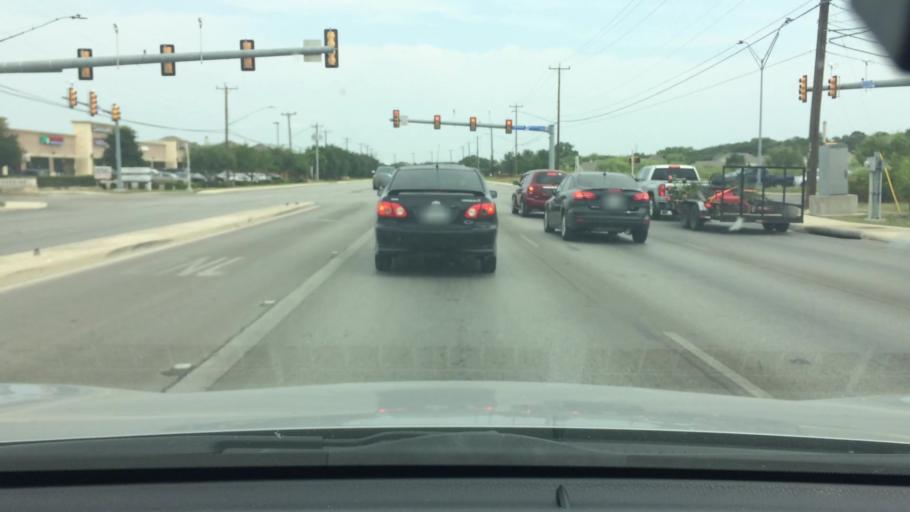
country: US
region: Texas
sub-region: Bexar County
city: Leon Valley
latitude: 29.4783
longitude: -98.6639
